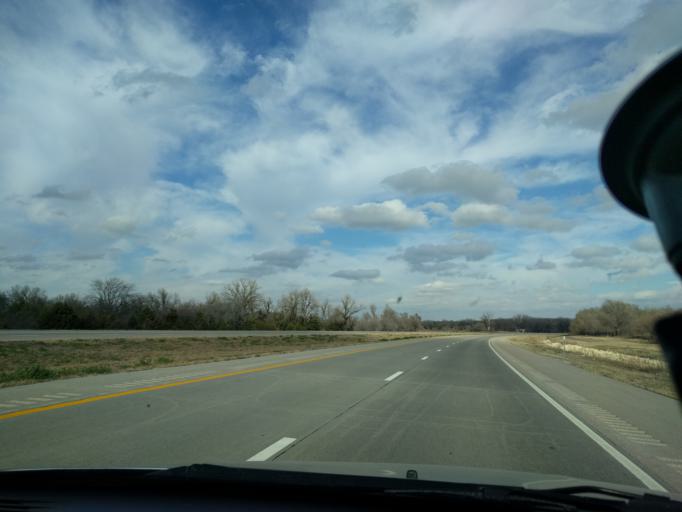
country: US
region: Kansas
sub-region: Reno County
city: Hutchinson
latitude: 38.1415
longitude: -97.8726
